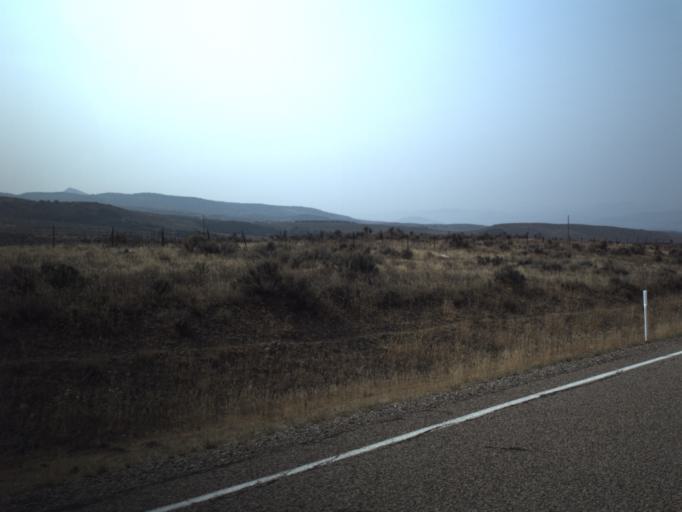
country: US
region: Utah
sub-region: Morgan County
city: Morgan
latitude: 40.9485
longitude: -111.5516
